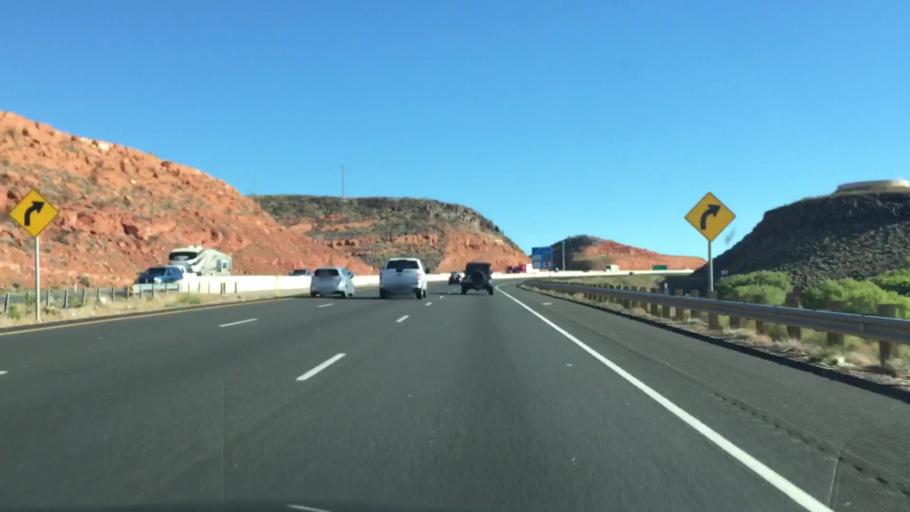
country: US
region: Utah
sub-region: Washington County
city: Washington
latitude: 37.1564
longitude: -113.4770
